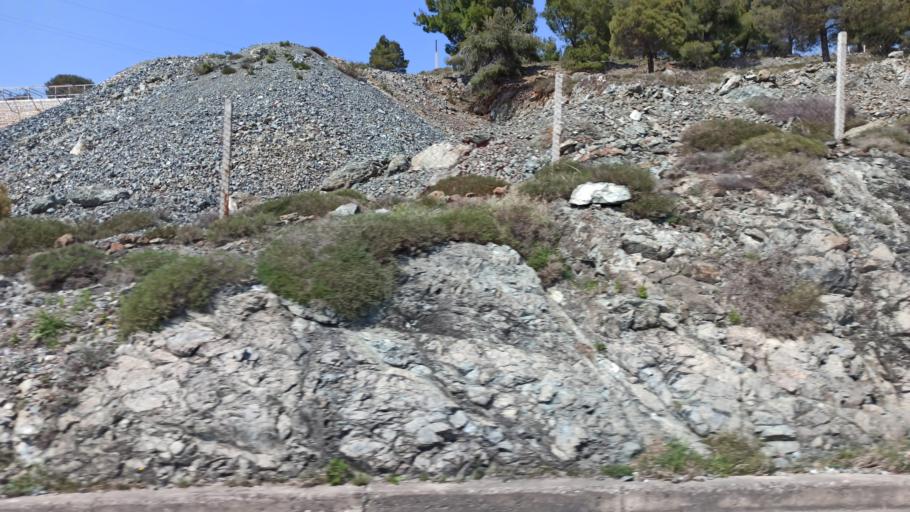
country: AL
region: Shkoder
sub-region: Rrethi i Malesia e Madhe
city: Kuc
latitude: 42.0541
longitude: 19.5357
